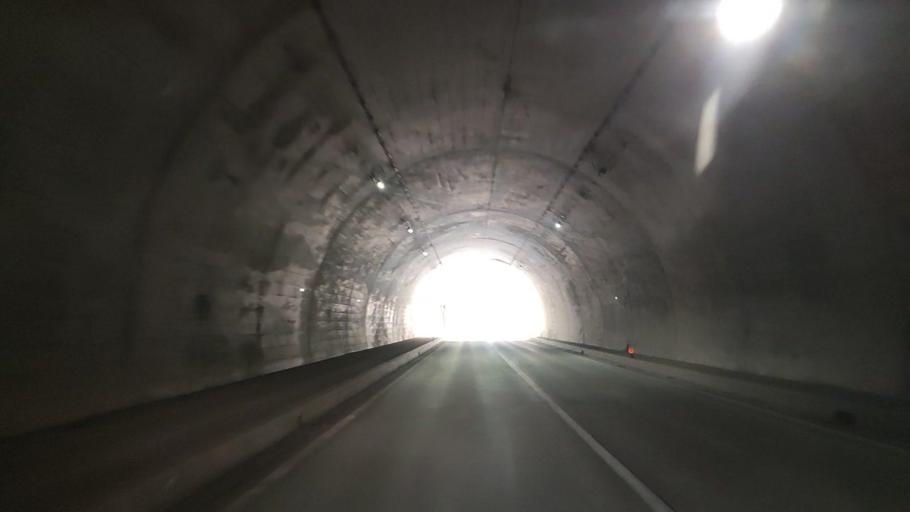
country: JP
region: Gifu
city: Takayama
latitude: 36.3359
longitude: 137.3005
